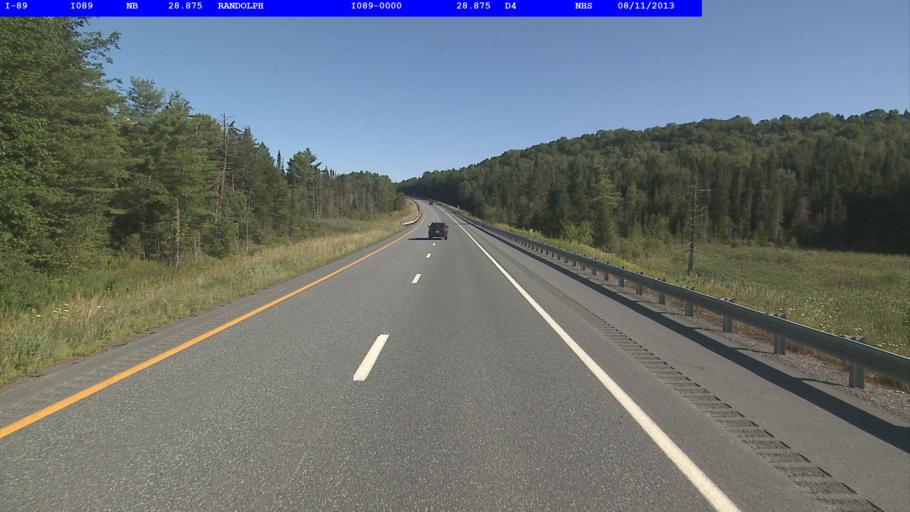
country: US
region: Vermont
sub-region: Orange County
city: Randolph
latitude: 43.9162
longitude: -72.6126
